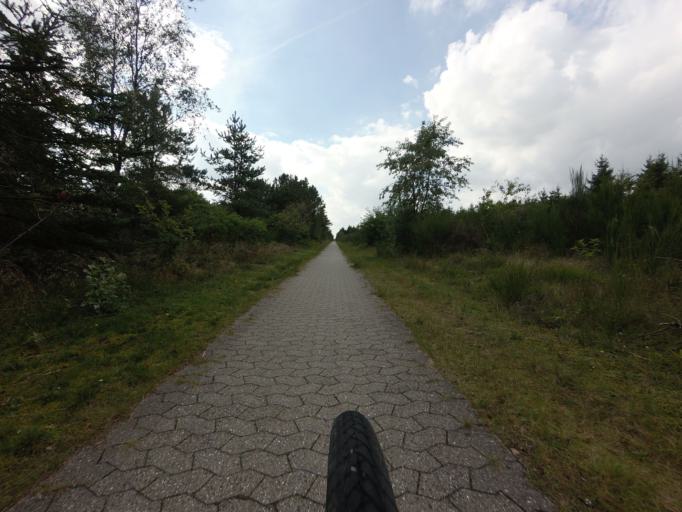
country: DK
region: Central Jutland
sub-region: Viborg Kommune
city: Karup
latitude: 56.3206
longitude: 9.2078
